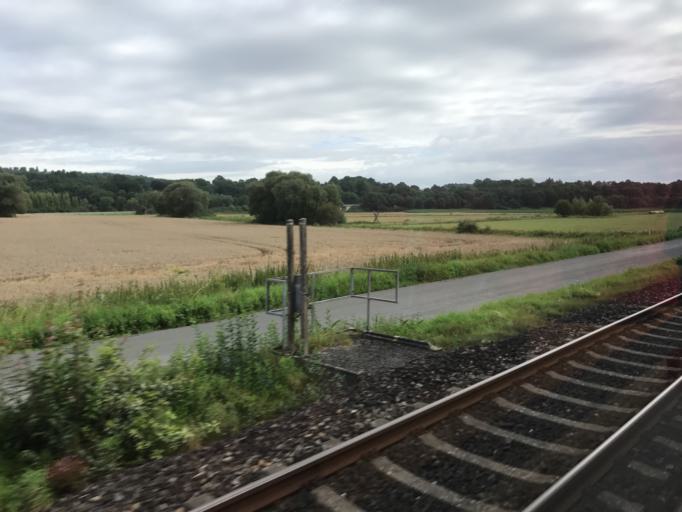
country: DE
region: Hesse
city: Selters
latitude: 50.5279
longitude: 8.2883
